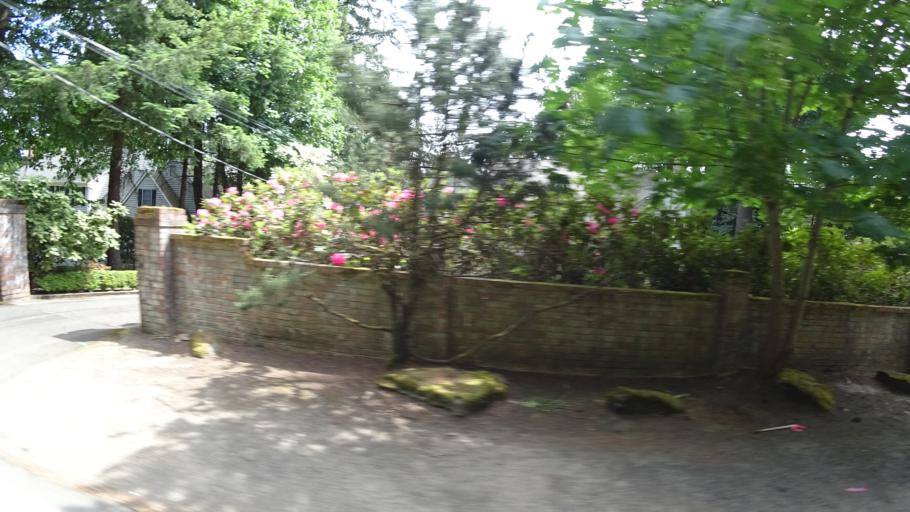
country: US
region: Oregon
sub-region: Clackamas County
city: Lake Oswego
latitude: 45.4458
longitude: -122.6696
